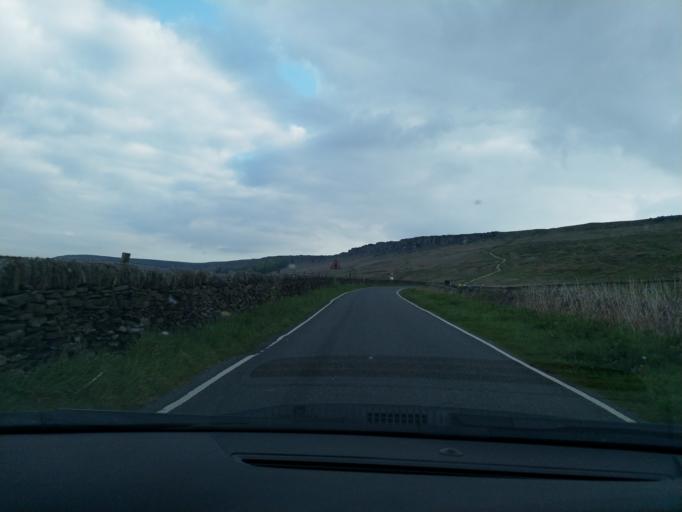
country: GB
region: England
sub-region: Derbyshire
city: Hathersage
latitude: 53.3404
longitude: -1.6338
